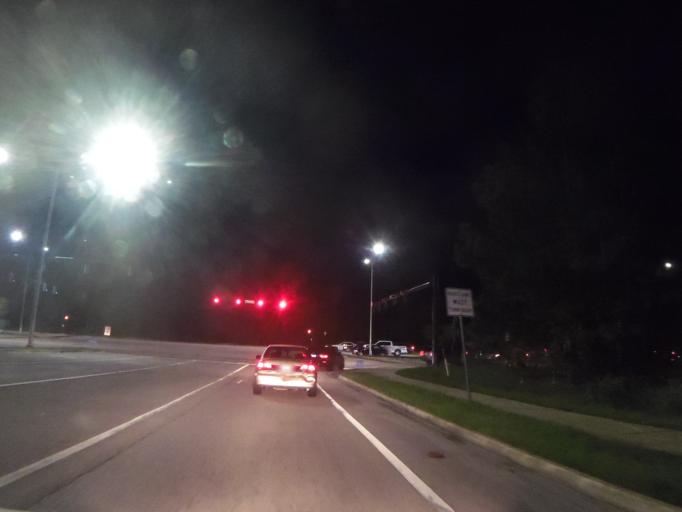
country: US
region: Florida
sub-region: Duval County
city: Jacksonville Beach
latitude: 30.2654
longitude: -81.5268
